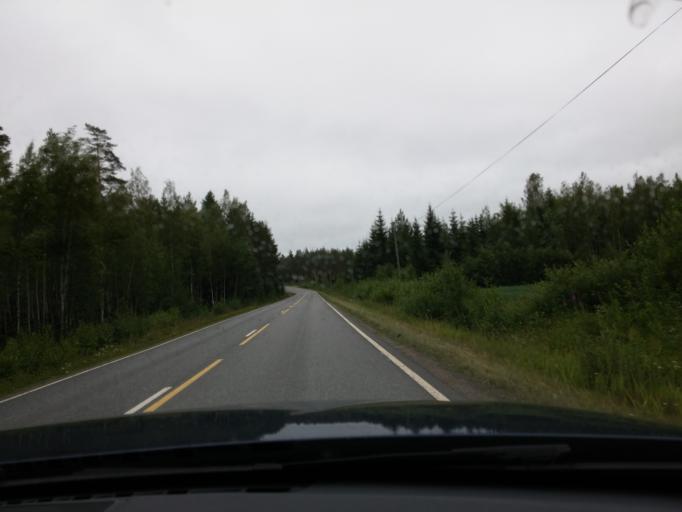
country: FI
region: Central Finland
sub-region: Joutsa
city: Joutsa
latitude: 61.7947
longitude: 26.0068
